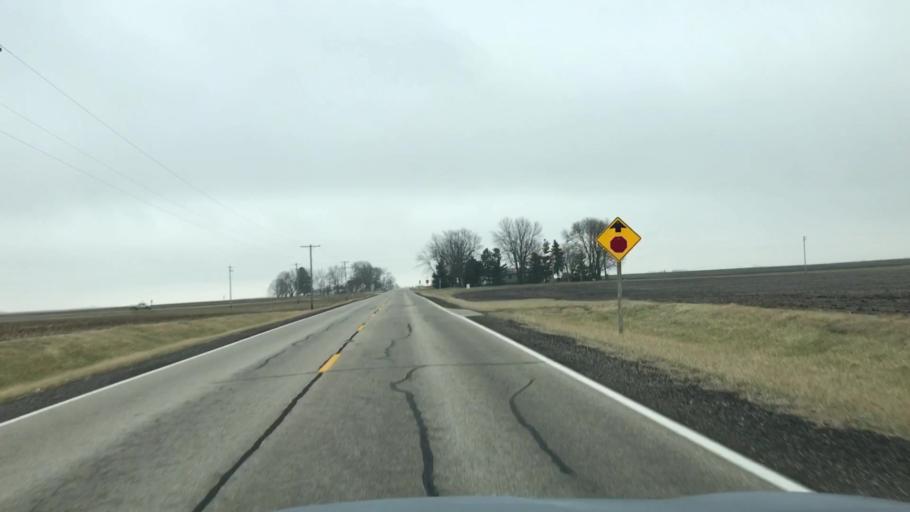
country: US
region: Illinois
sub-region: McLean County
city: Hudson
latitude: 40.6079
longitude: -88.9452
